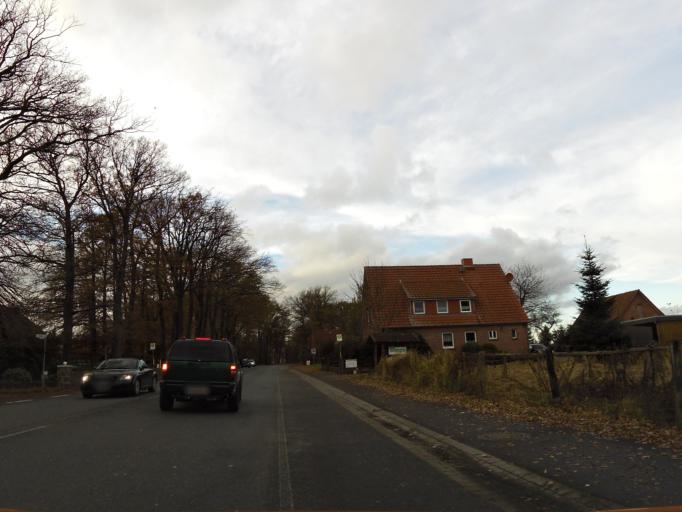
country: DE
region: Lower Saxony
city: Bispingen
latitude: 53.0150
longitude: 10.0181
